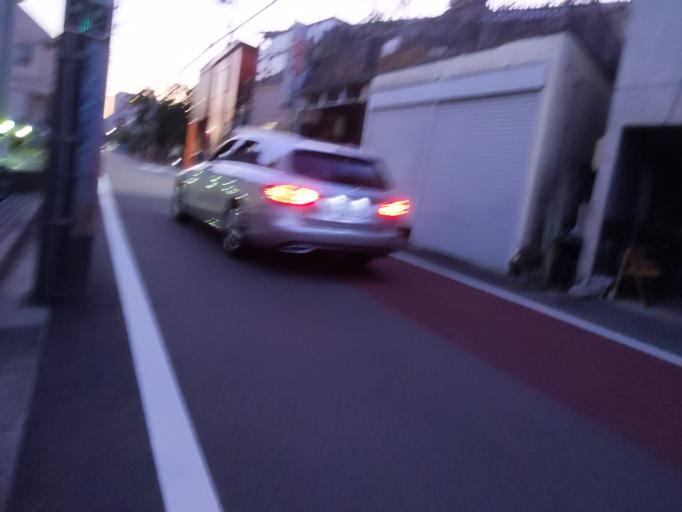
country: JP
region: Tokyo
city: Mitaka-shi
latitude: 35.6521
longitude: 139.6207
